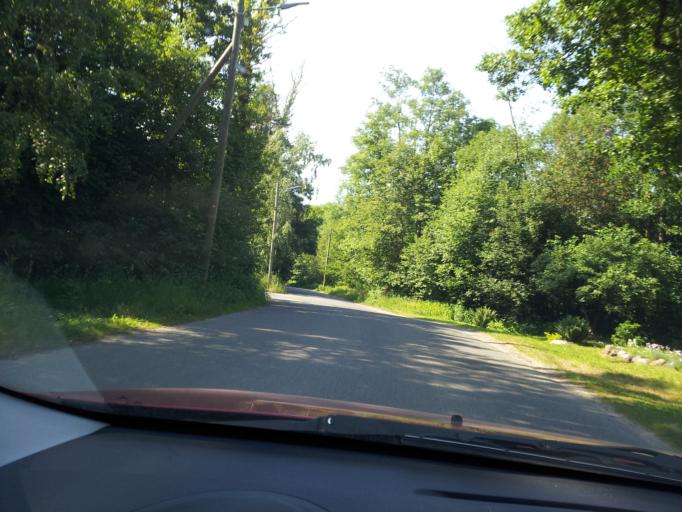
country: LV
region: Riga
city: Daugavgriva
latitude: 57.0610
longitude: 24.0562
